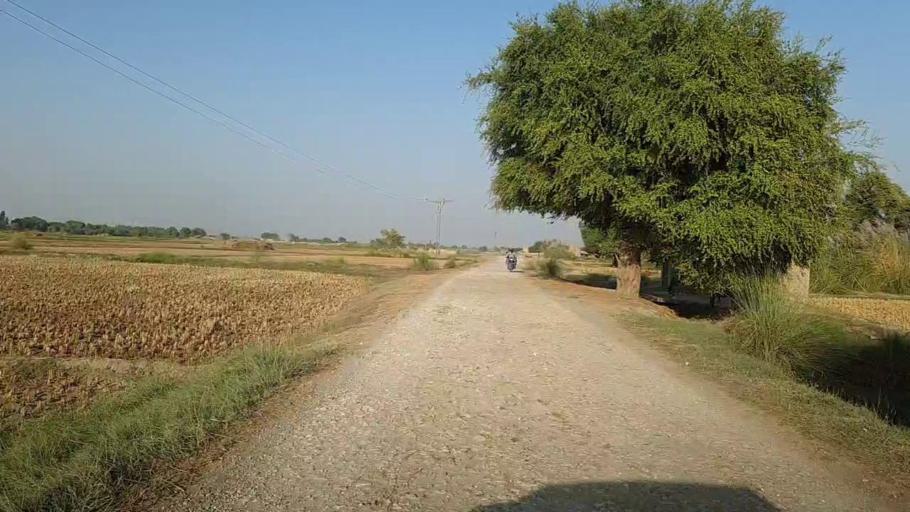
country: PK
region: Sindh
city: Kashmor
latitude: 28.4214
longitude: 69.4204
